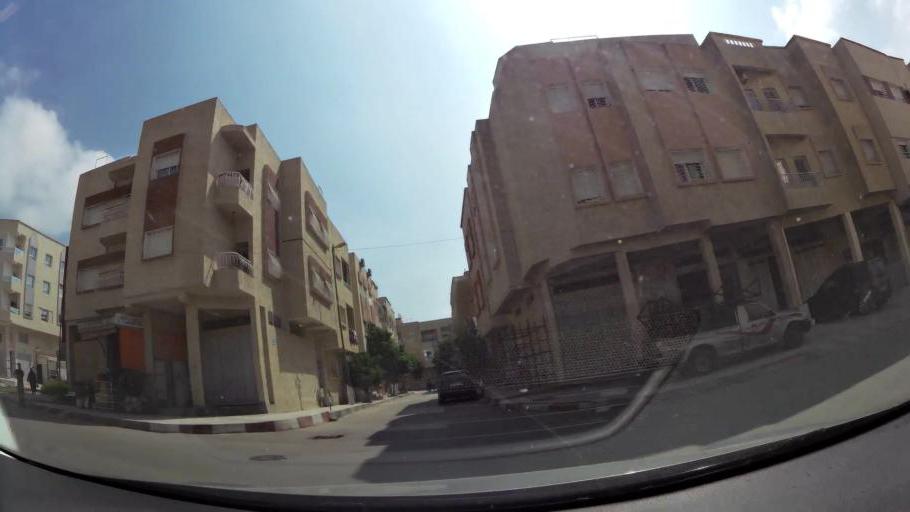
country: MA
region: Fes-Boulemane
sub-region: Fes
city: Fes
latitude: 34.0583
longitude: -5.0262
